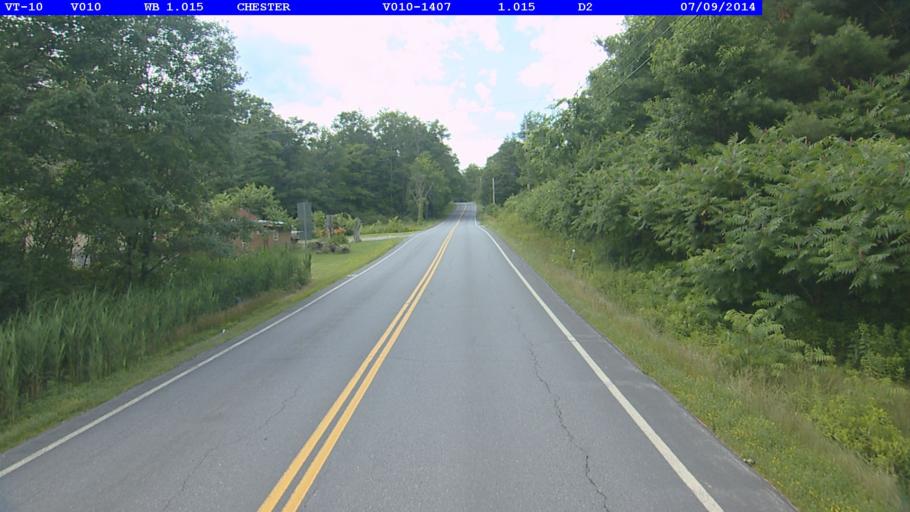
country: US
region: Vermont
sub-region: Windsor County
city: Chester
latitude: 43.3272
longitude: -72.5878
